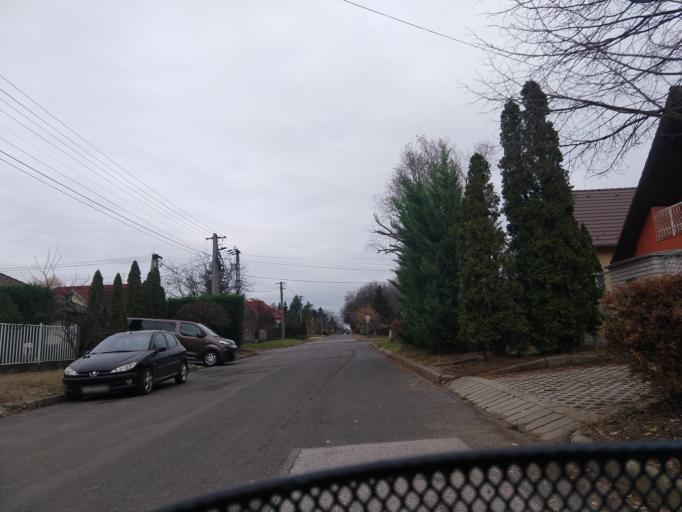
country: HU
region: Pest
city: Orbottyan
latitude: 47.6710
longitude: 19.2887
